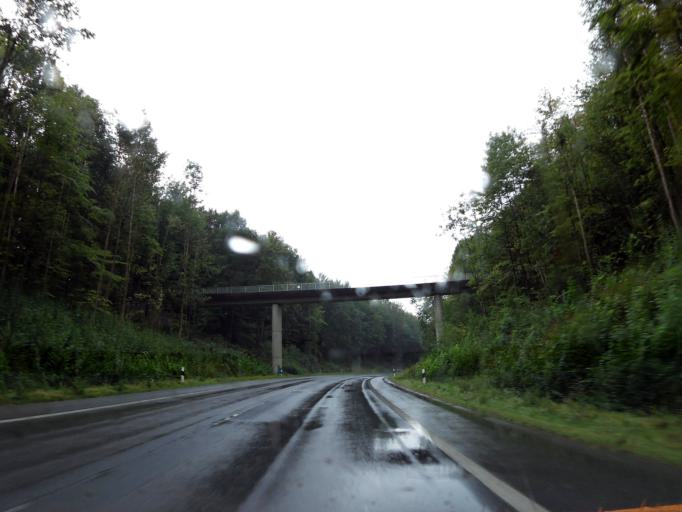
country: DE
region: Lower Saxony
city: Wollershausen
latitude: 51.6238
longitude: 10.2660
